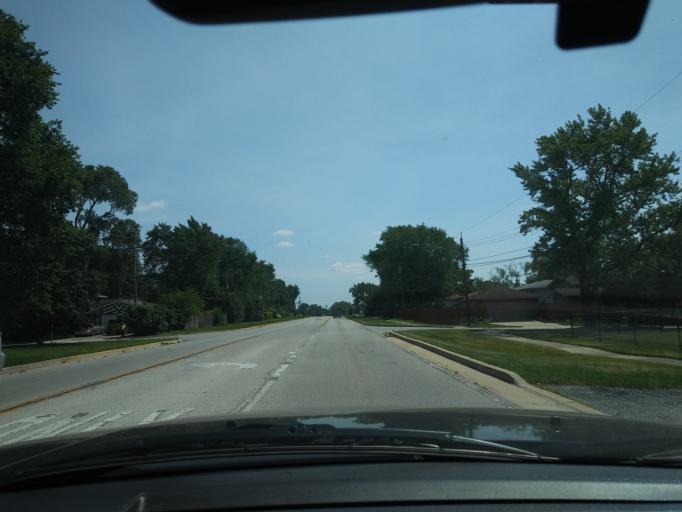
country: US
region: Illinois
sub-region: Cook County
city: Oak Forest
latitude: 41.6207
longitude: -87.7567
